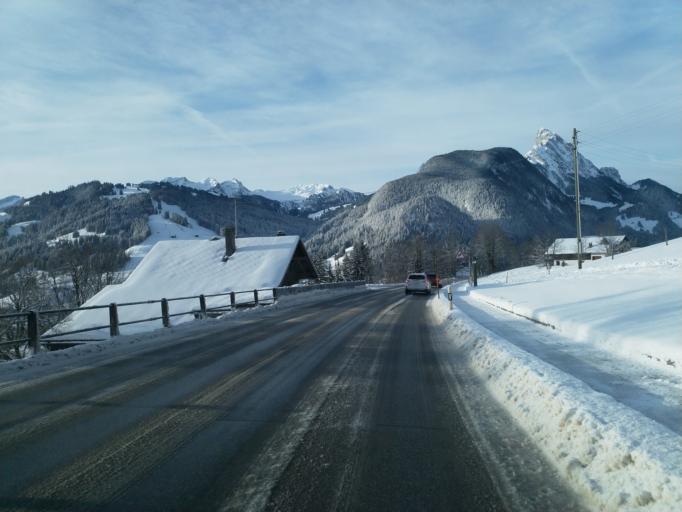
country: CH
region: Bern
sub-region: Obersimmental-Saanen District
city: Saanen
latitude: 46.4940
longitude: 7.2730
